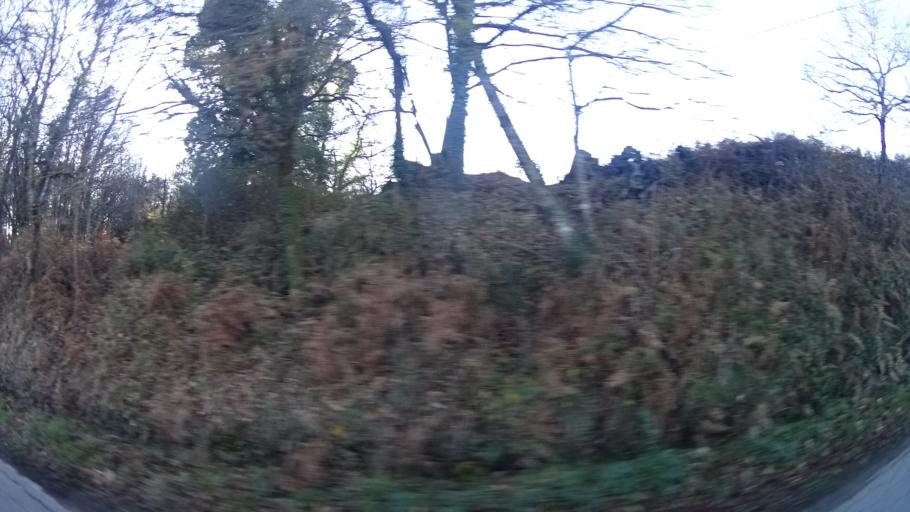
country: FR
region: Brittany
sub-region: Departement du Morbihan
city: Allaire
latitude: 47.6551
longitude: -2.1581
